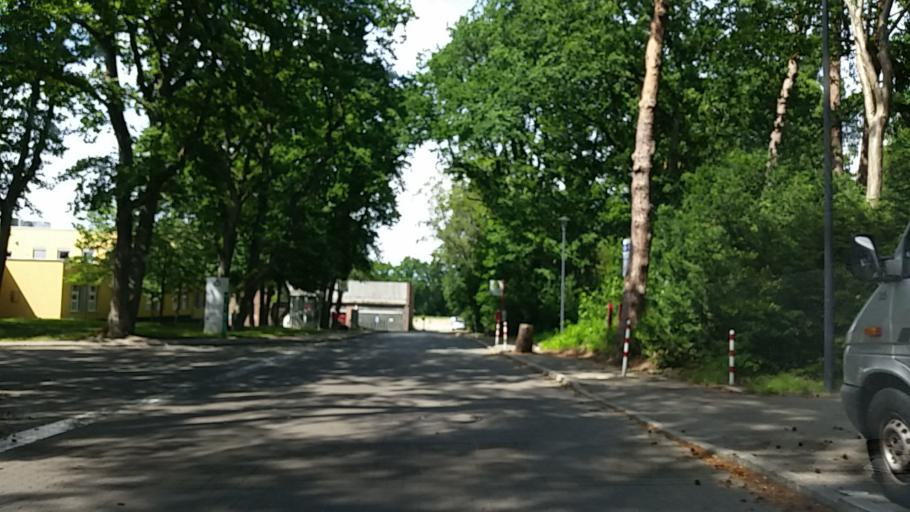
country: DE
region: Schleswig-Holstein
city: Rellingen
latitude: 53.5821
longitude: 9.7790
